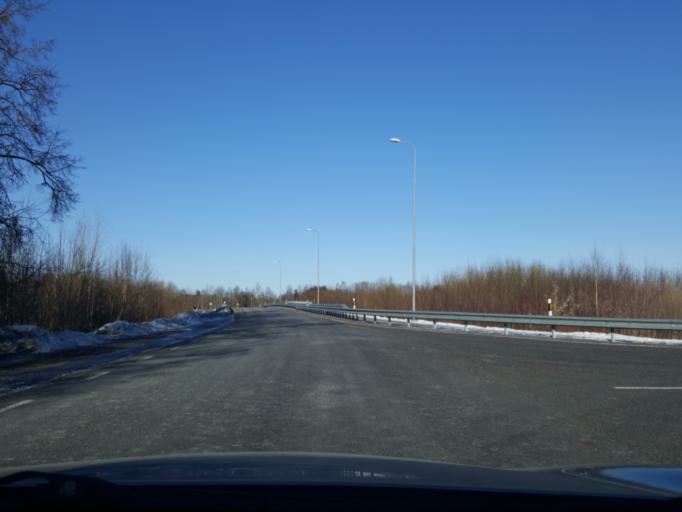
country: EE
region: Viljandimaa
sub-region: Vohma linn
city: Vohma
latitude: 58.5616
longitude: 25.5522
